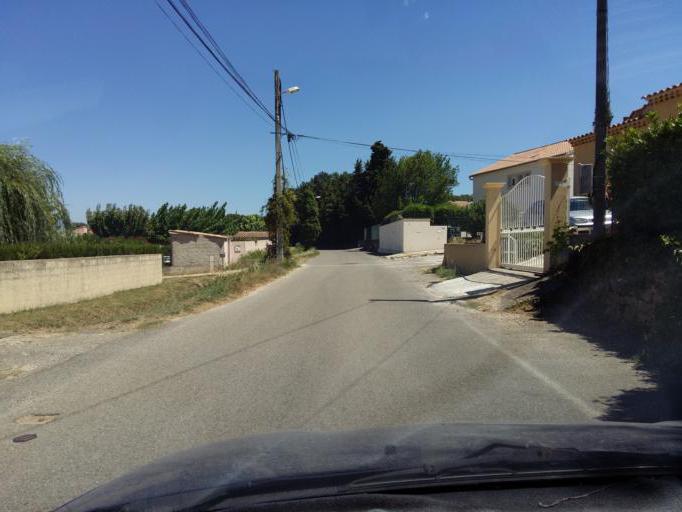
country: FR
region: Provence-Alpes-Cote d'Azur
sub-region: Departement du Vaucluse
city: Piolenc
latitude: 44.1764
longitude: 4.7679
